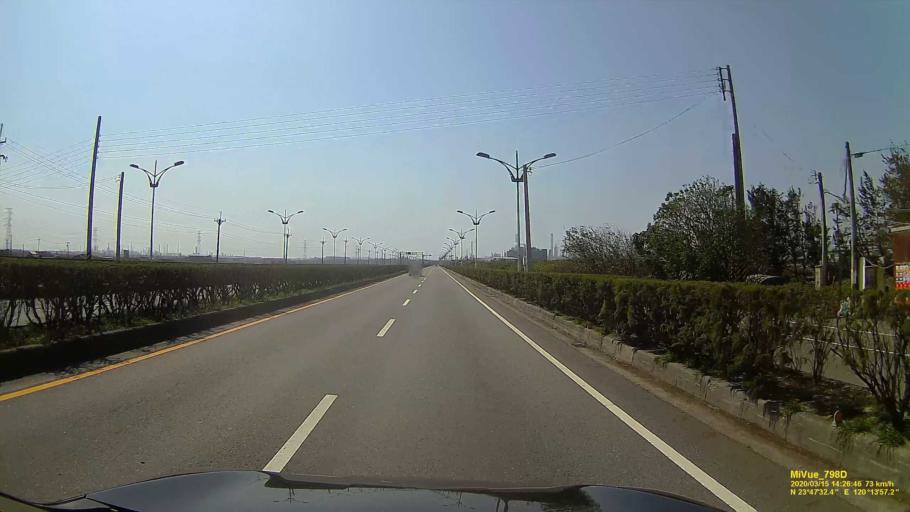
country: TW
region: Taiwan
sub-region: Yunlin
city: Douliu
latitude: 23.7924
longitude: 120.2322
